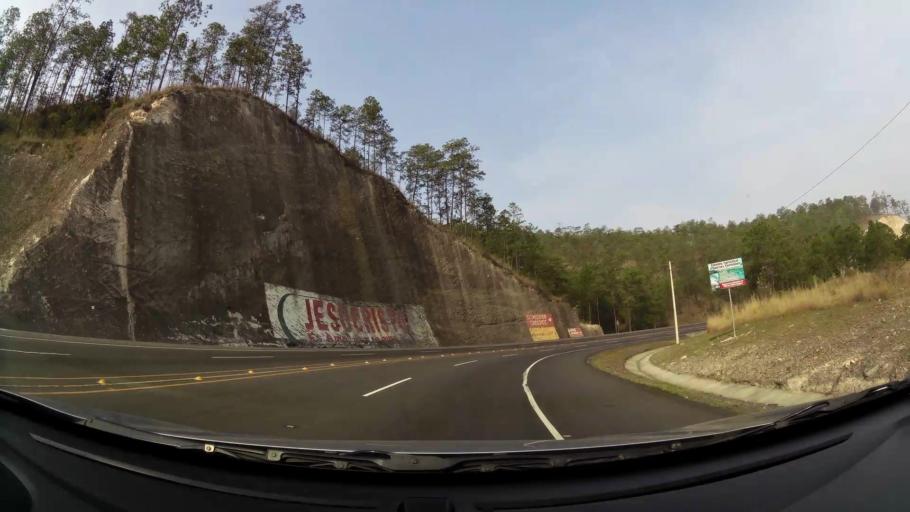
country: HN
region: Francisco Morazan
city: Zambrano
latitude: 14.2814
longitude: -87.4671
